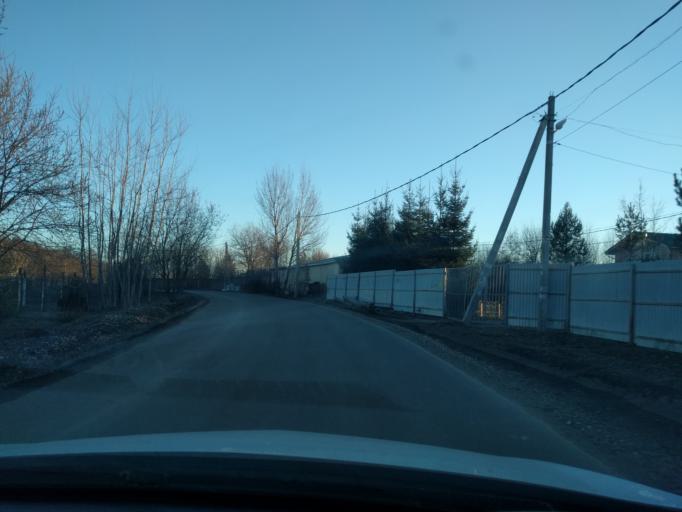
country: RU
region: Moskovskaya
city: Dubrovitsy
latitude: 55.4879
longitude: 37.4418
